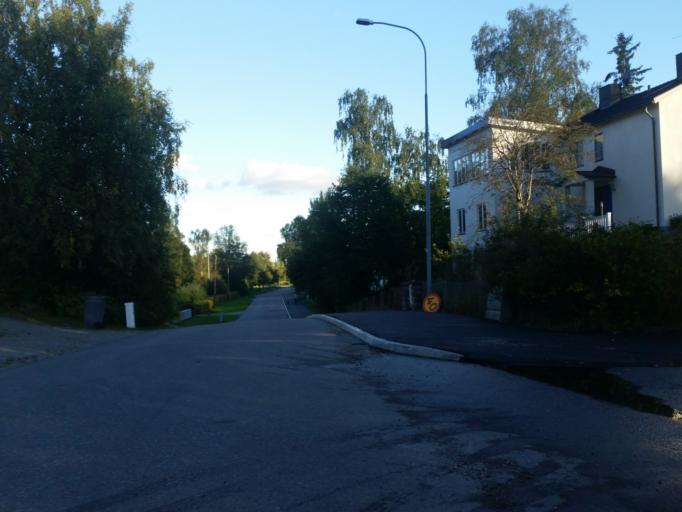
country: SE
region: Stockholm
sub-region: Norrtalje Kommun
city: Bergshamra
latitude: 59.4094
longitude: 18.0143
